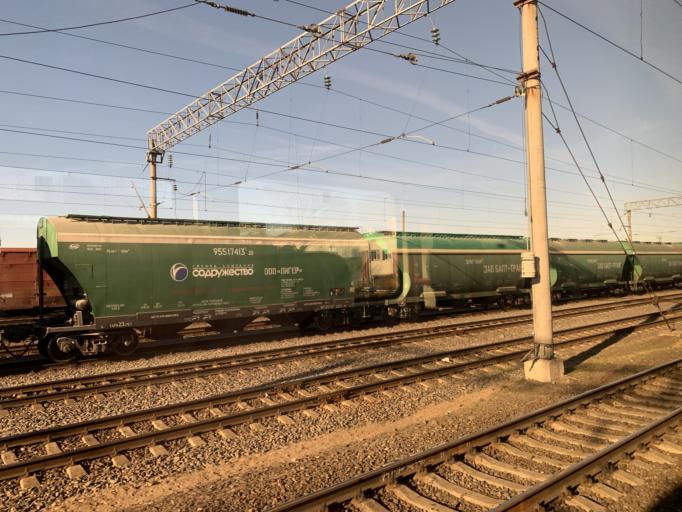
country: BY
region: Minsk
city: Maladzyechna
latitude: 54.3166
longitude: 26.8292
